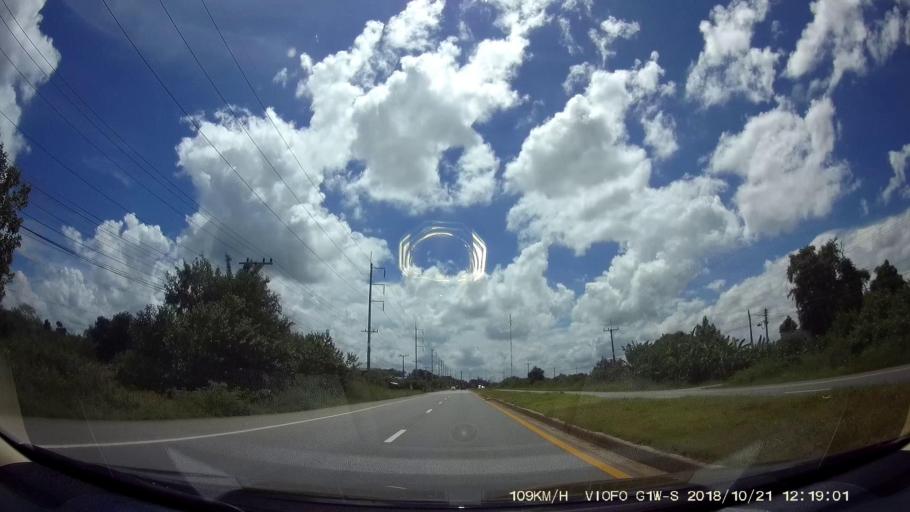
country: TH
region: Nakhon Ratchasima
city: Dan Khun Thot
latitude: 15.3072
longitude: 101.8155
